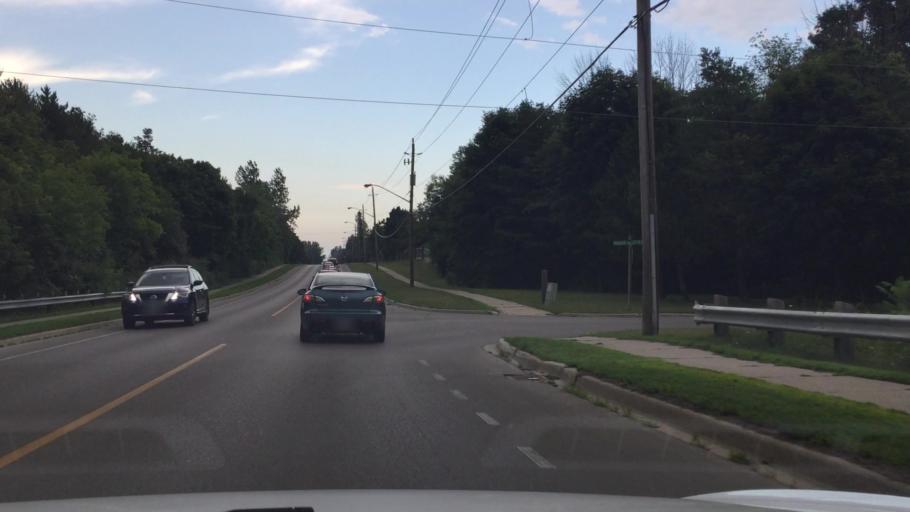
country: CA
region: Ontario
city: Oshawa
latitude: 43.9117
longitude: -78.7999
